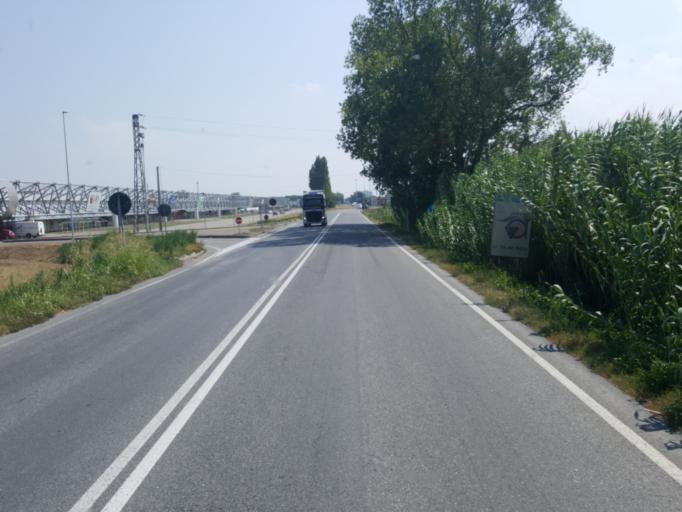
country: IT
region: Emilia-Romagna
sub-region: Provincia di Ravenna
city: Ravenna
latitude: 44.4544
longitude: 12.2095
